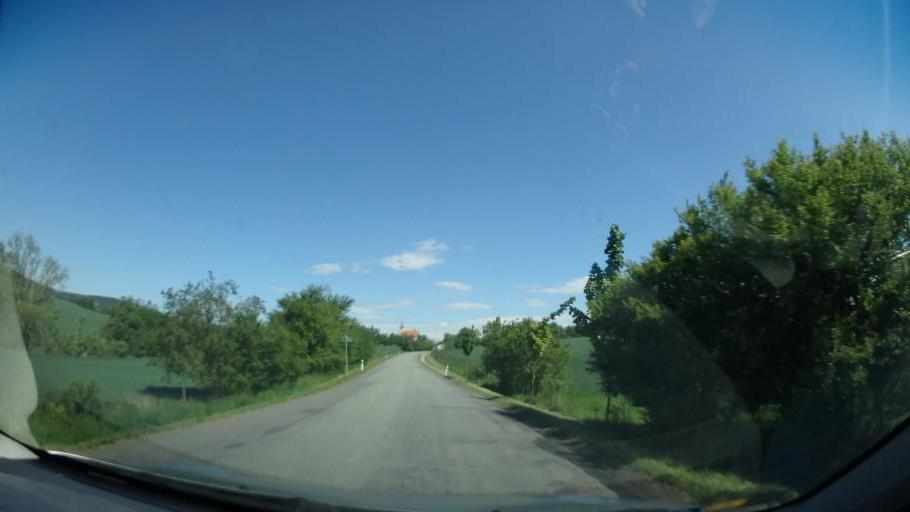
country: CZ
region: South Moravian
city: Velke Opatovice
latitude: 49.6740
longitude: 16.6318
